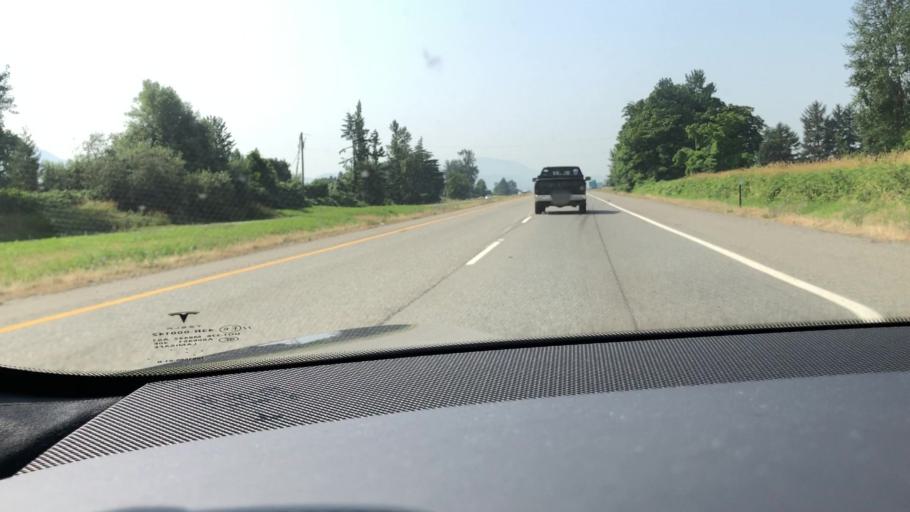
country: CA
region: British Columbia
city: Abbotsford
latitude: 49.1061
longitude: -122.1113
